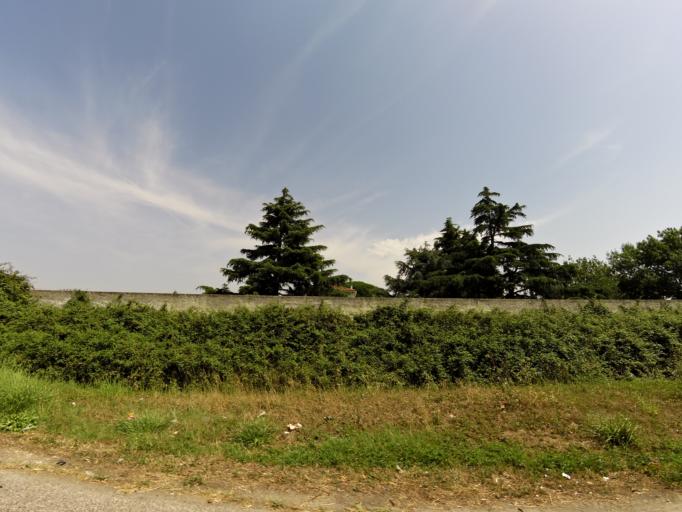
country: FR
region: Provence-Alpes-Cote d'Azur
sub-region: Departement du Var
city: Hyeres
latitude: 43.1151
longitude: 6.1148
